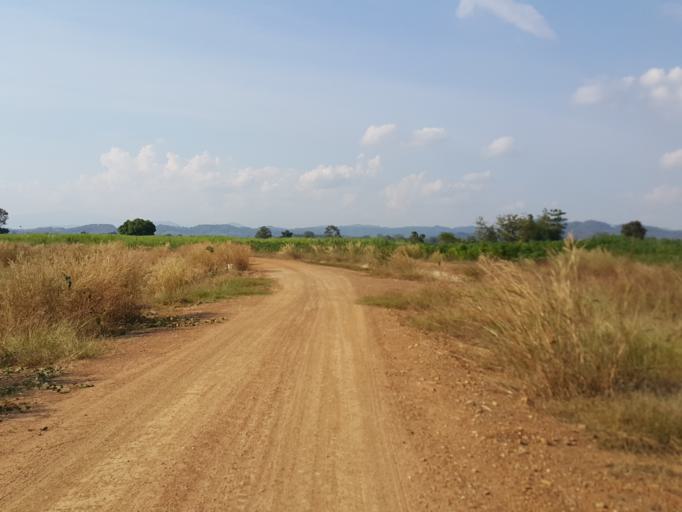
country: TH
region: Sukhothai
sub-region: Amphoe Si Satchanalai
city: Si Satchanalai
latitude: 17.4732
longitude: 99.6590
